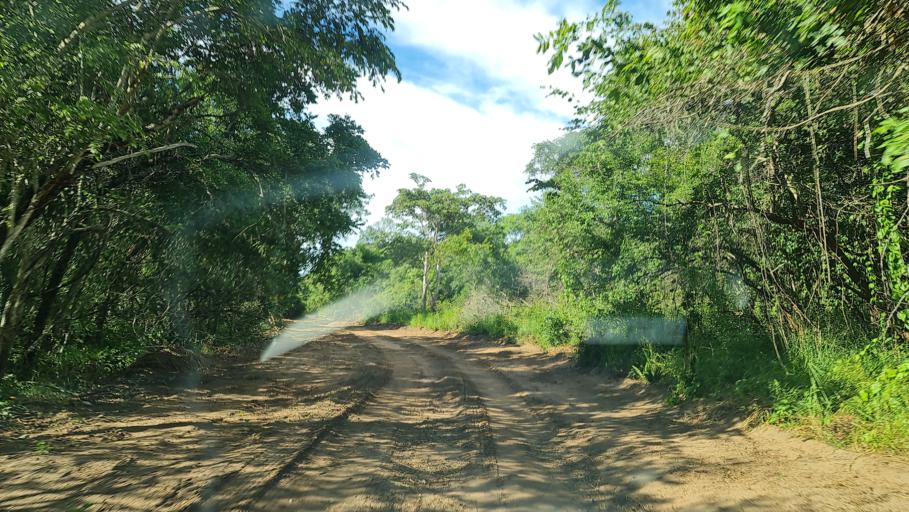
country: MZ
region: Nampula
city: Antonio Enes
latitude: -15.5292
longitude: 40.1265
